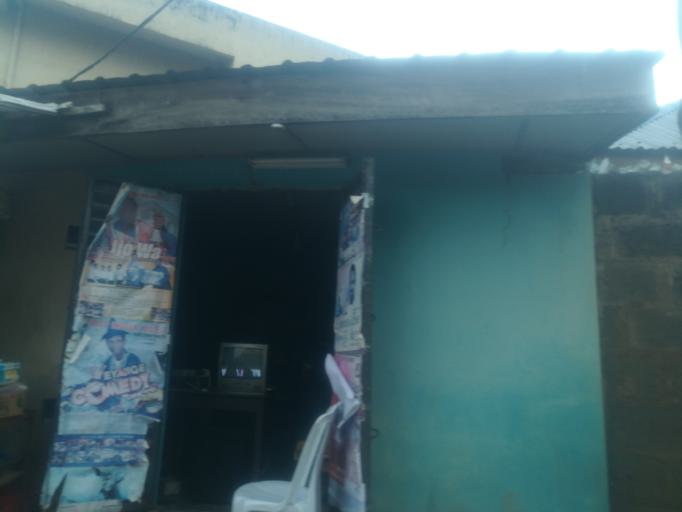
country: NG
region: Oyo
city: Ibadan
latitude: 7.3788
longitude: 3.8545
